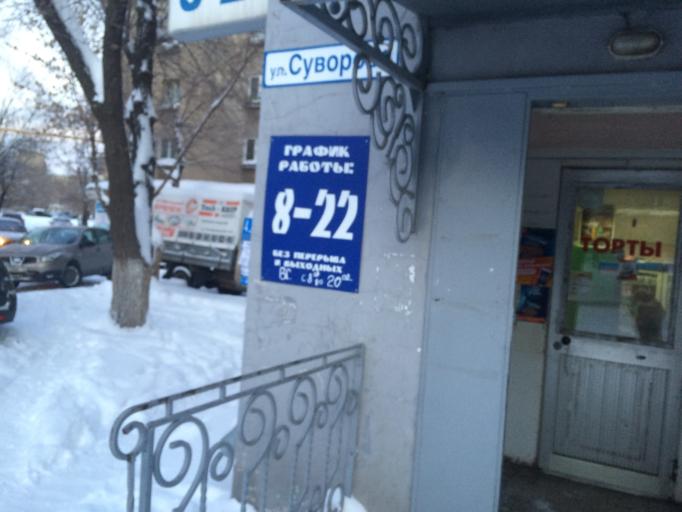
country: RU
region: Chelyabinsk
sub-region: Gorod Magnitogorsk
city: Magnitogorsk
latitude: 53.4060
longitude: 58.9718
